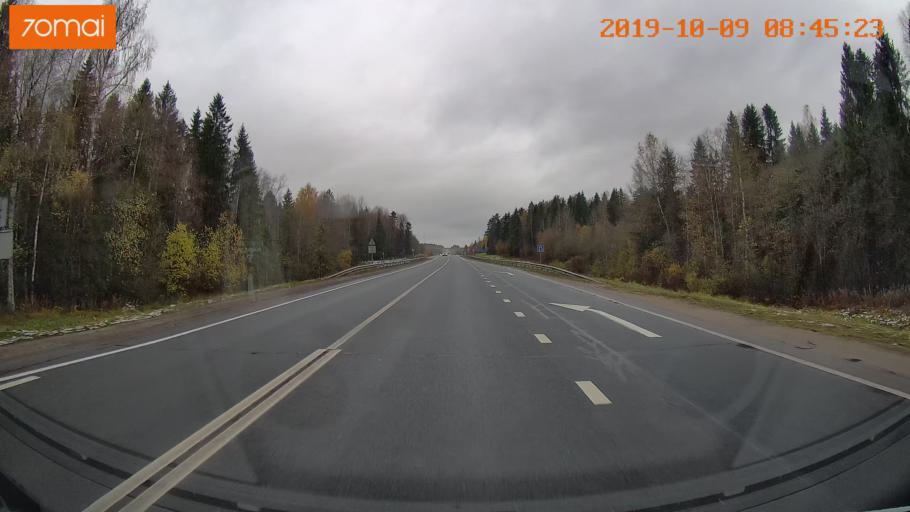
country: RU
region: Vologda
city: Gryazovets
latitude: 59.0475
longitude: 40.0914
